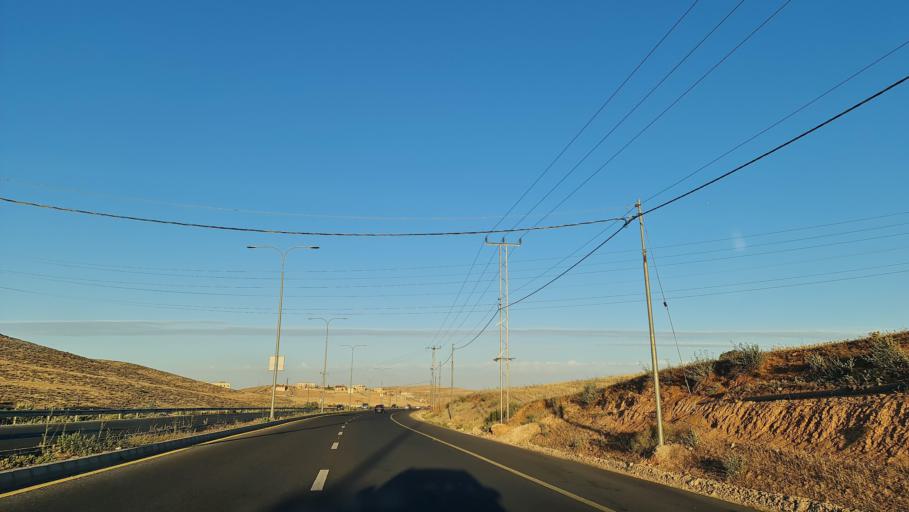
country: JO
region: Zarqa
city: Russeifa
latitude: 32.0880
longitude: 35.9954
